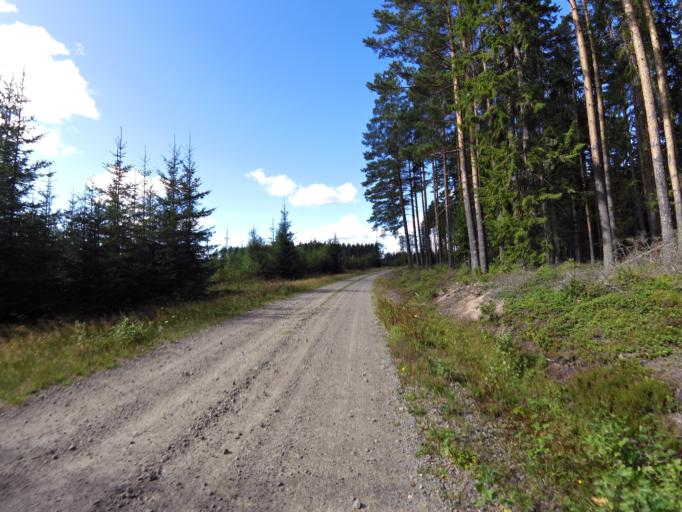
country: SE
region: Gaevleborg
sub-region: Ockelbo Kommun
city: Ockelbo
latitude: 60.8108
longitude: 16.7719
